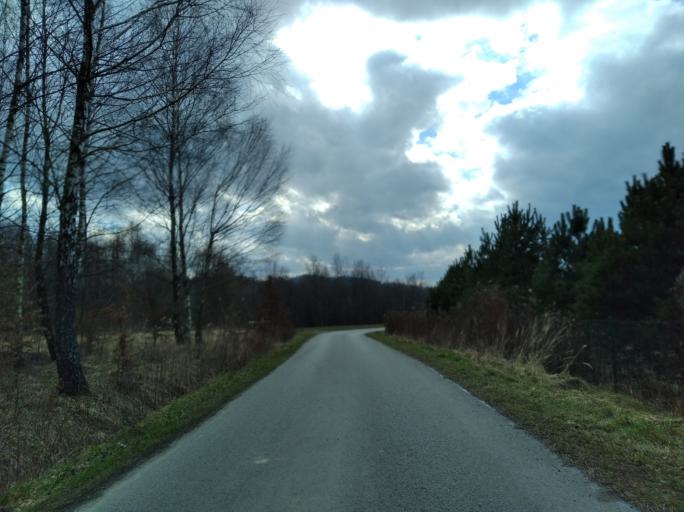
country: PL
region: Subcarpathian Voivodeship
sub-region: Powiat strzyzowski
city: Wysoka Strzyzowska
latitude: 49.7944
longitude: 21.7279
